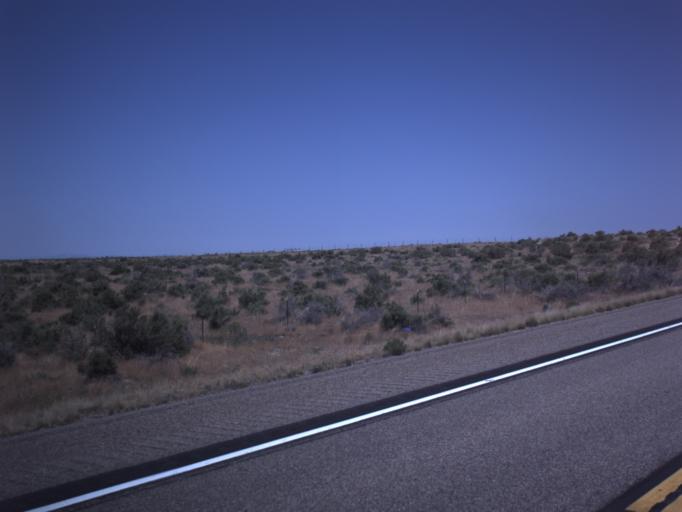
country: US
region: Utah
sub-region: Millard County
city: Delta
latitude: 39.3719
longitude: -112.4964
